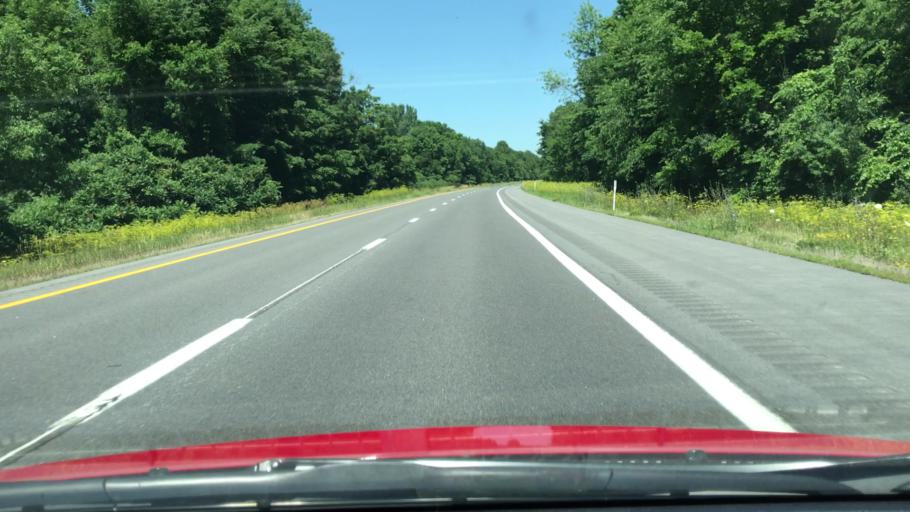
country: US
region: New York
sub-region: Clinton County
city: Champlain
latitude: 44.8529
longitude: -73.4491
